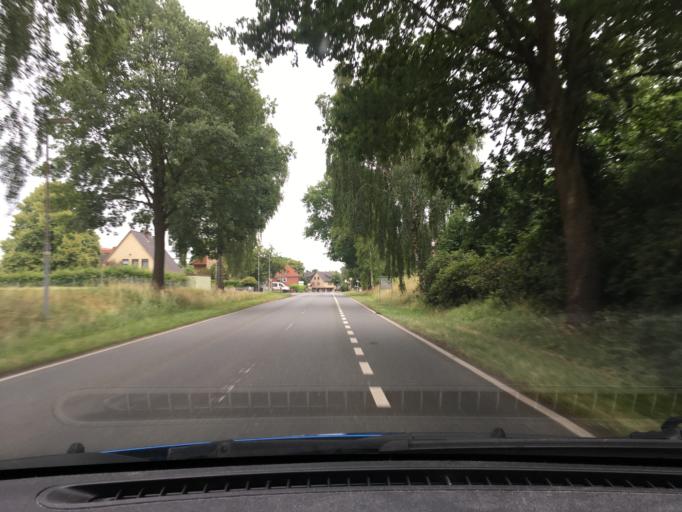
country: DE
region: Lower Saxony
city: Bispingen
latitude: 53.0872
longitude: 9.9916
